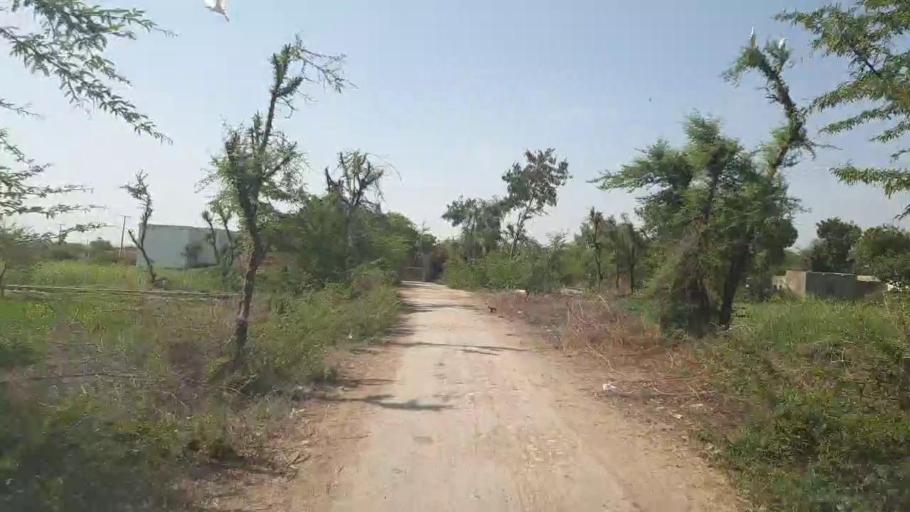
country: PK
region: Sindh
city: Kunri
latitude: 25.2667
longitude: 69.6363
